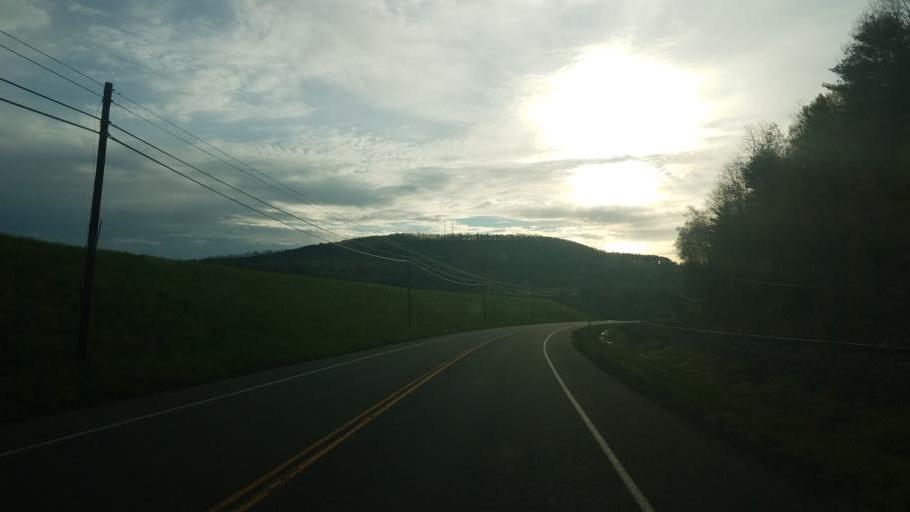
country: US
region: New York
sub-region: Steuben County
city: Hornell
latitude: 42.3442
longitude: -77.7105
